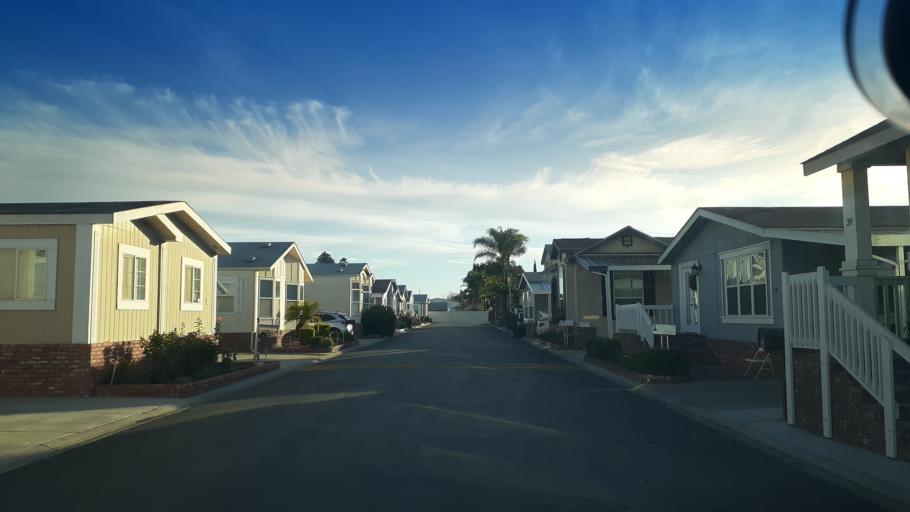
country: US
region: California
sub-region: Los Angeles County
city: Artesia
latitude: 33.8567
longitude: -118.0843
